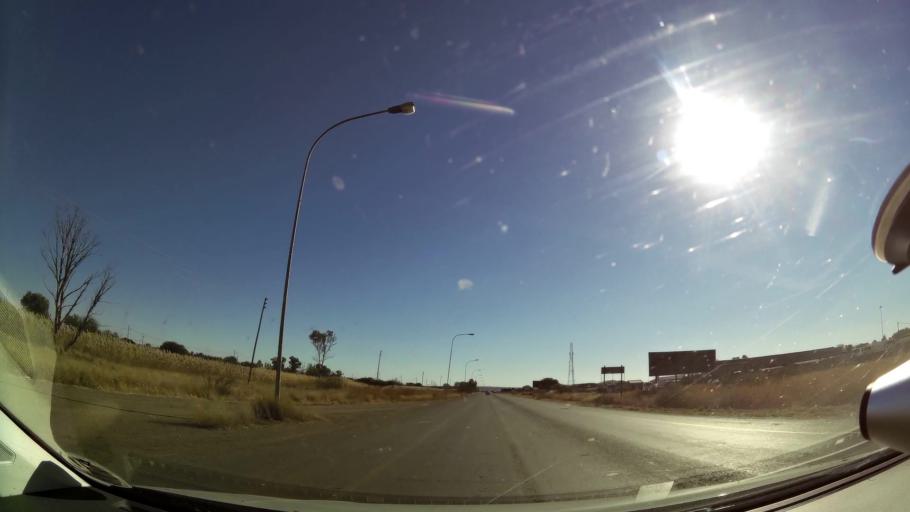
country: ZA
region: Northern Cape
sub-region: Frances Baard District Municipality
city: Kimberley
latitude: -28.7044
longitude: 24.7769
